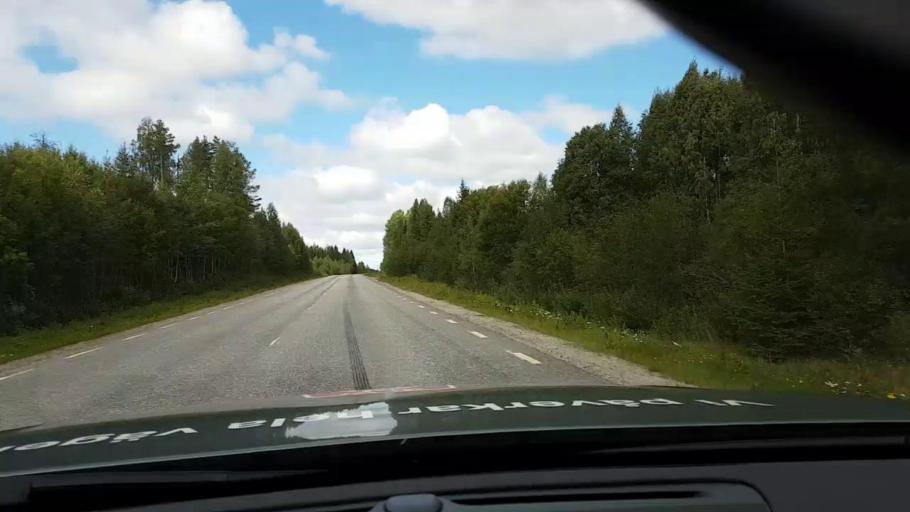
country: SE
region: Vaesternorrland
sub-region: OErnskoeldsviks Kommun
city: Bredbyn
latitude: 63.4709
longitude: 18.0996
